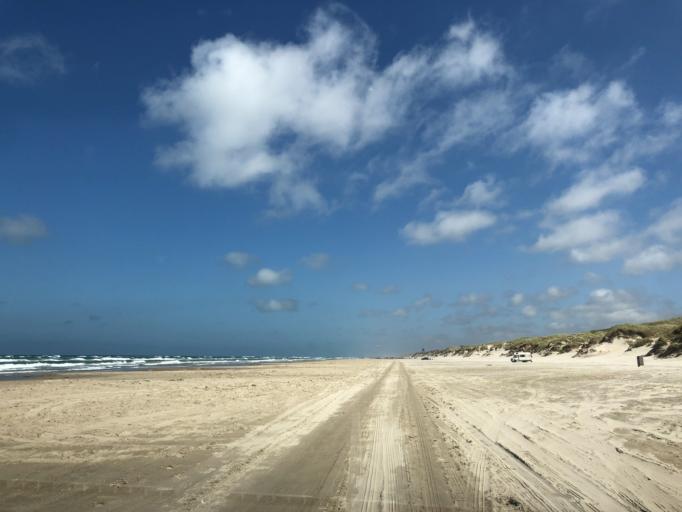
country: DK
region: North Denmark
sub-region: Jammerbugt Kommune
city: Pandrup
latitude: 57.2440
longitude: 9.5654
